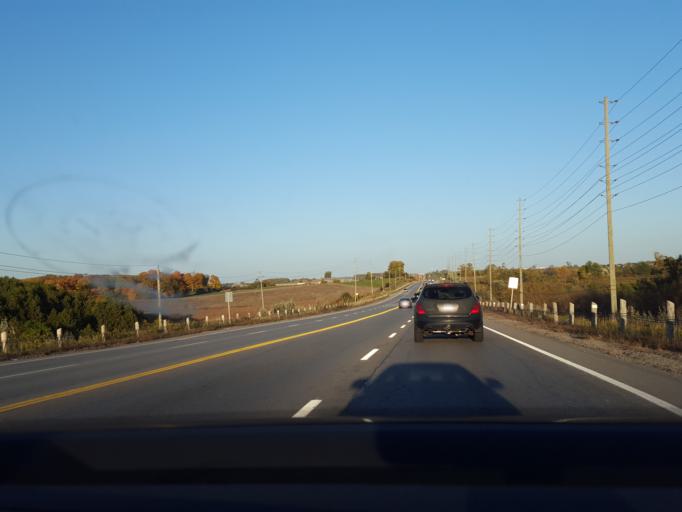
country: CA
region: Ontario
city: Newmarket
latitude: 44.0756
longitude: -79.4729
